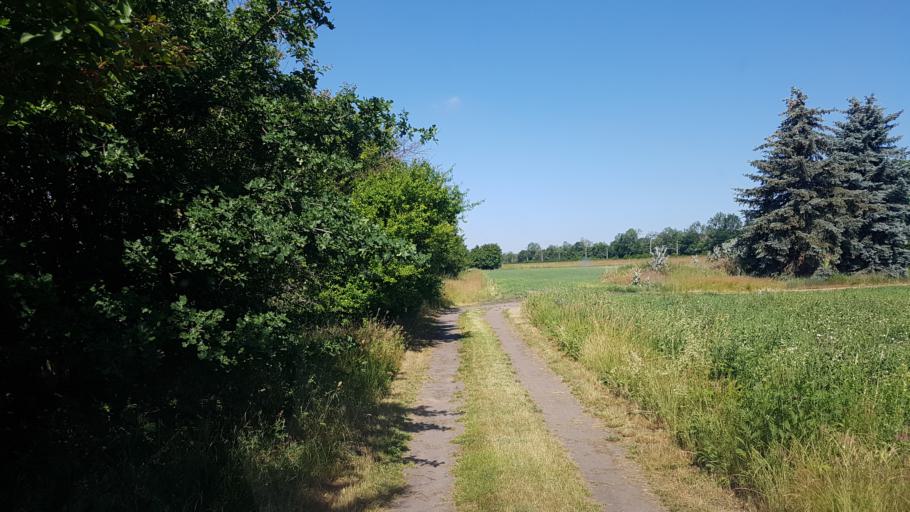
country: DE
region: Brandenburg
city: Plessa
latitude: 51.4697
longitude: 13.5978
